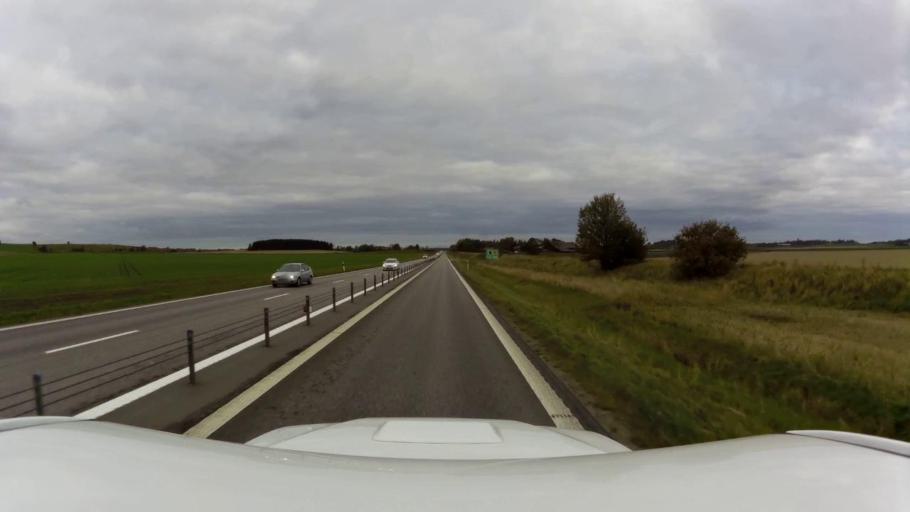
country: SE
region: OEstergoetland
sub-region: Linkopings Kommun
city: Berg
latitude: 58.4631
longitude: 15.4963
